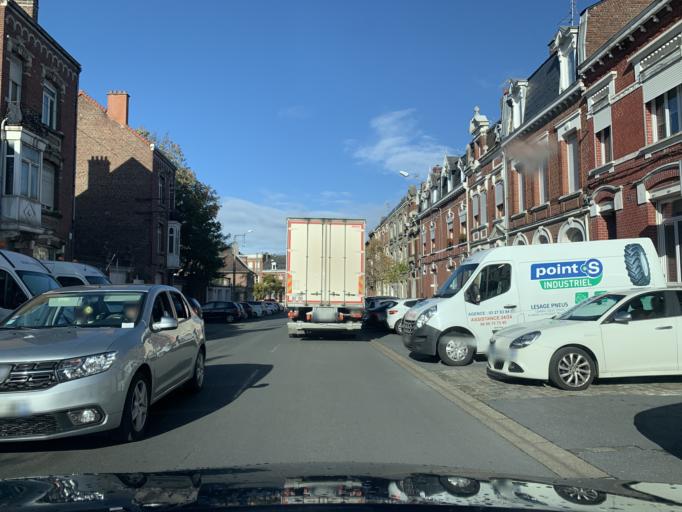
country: FR
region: Nord-Pas-de-Calais
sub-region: Departement du Nord
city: Cambrai
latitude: 50.1776
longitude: 3.2390
